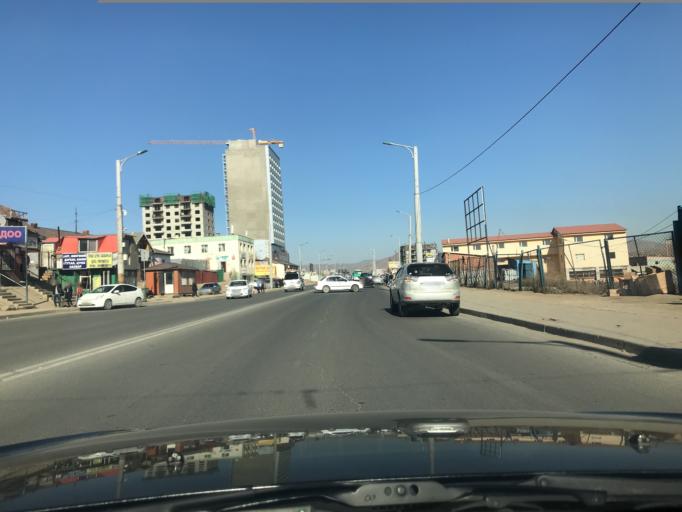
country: MN
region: Ulaanbaatar
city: Ulaanbaatar
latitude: 47.9326
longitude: 106.9057
